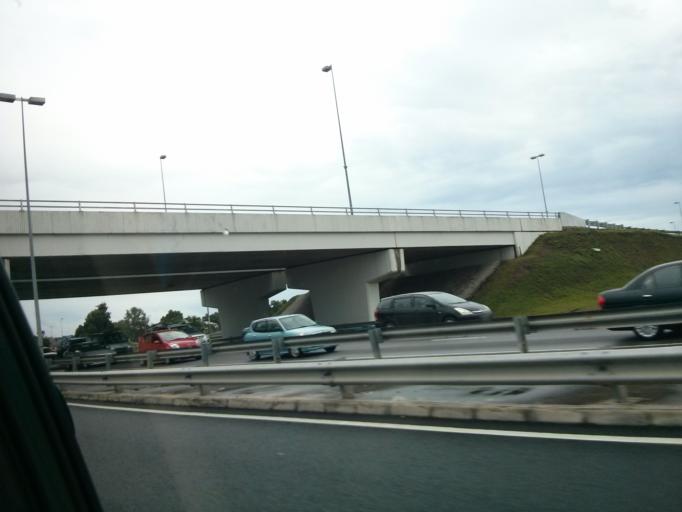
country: BN
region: Brunei and Muara
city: Bandar Seri Begawan
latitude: 4.9421
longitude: 114.9092
